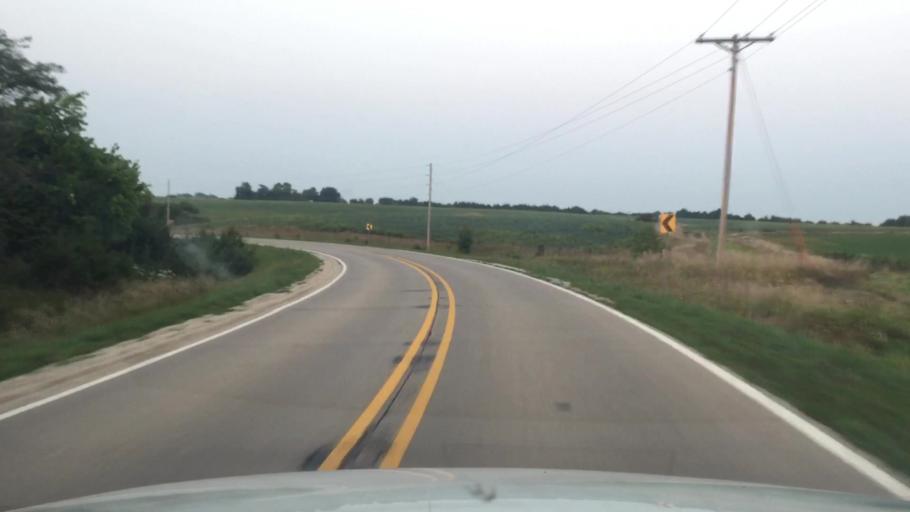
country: US
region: Iowa
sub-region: Clarke County
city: Osceola
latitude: 41.1839
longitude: -93.7011
